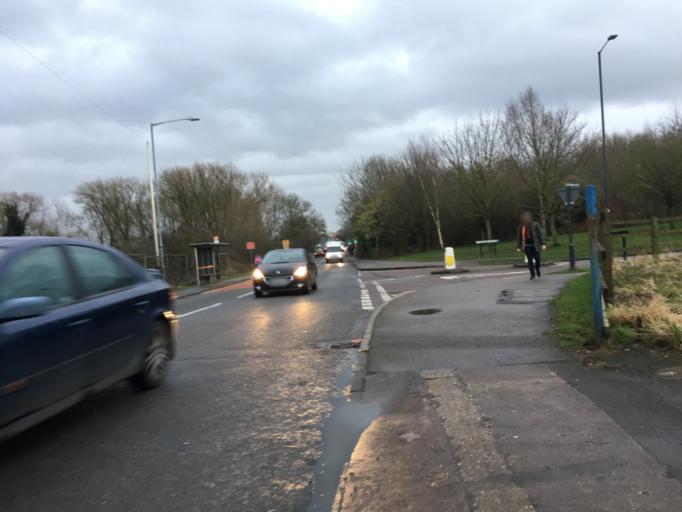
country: GB
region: England
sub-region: Warwickshire
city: Rugby
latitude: 52.3844
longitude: -1.2490
